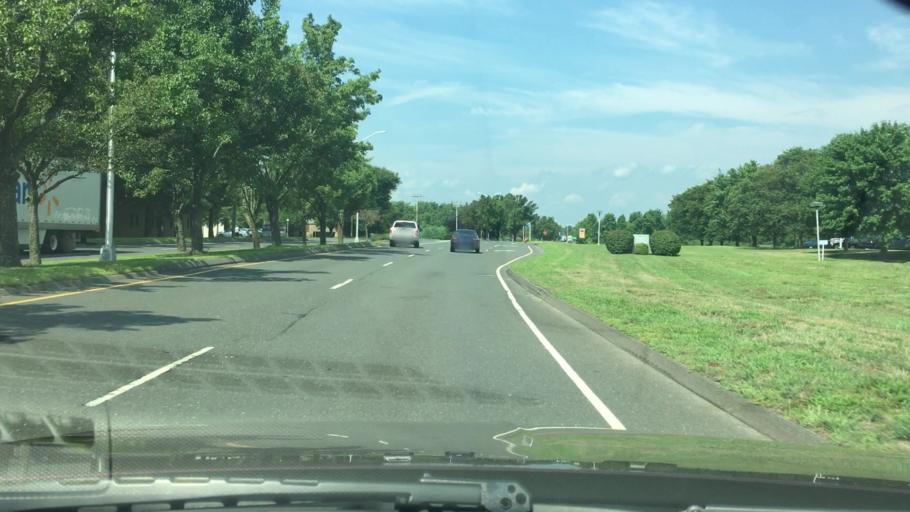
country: US
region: Connecticut
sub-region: Hartford County
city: Windsor
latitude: 41.8751
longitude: -72.6889
